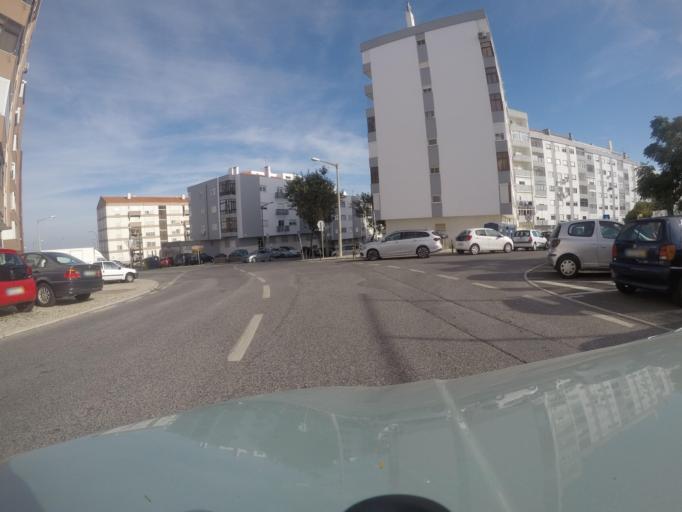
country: PT
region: Lisbon
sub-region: Amadora
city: Amadora
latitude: 38.7701
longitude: -9.2262
